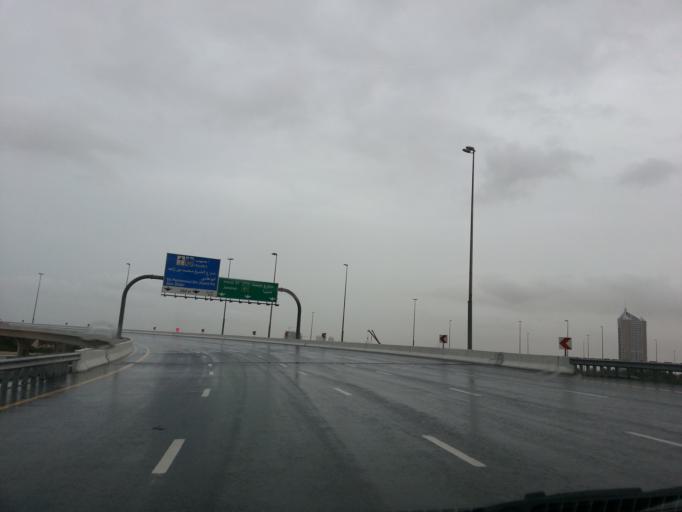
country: AE
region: Dubai
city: Dubai
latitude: 25.0514
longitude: 55.2259
